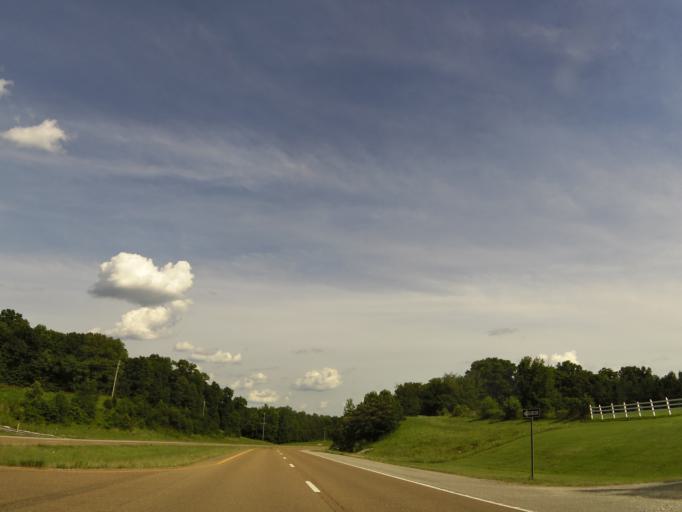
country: US
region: Tennessee
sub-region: Carroll County
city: Huntingdon
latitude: 36.0218
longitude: -88.3978
